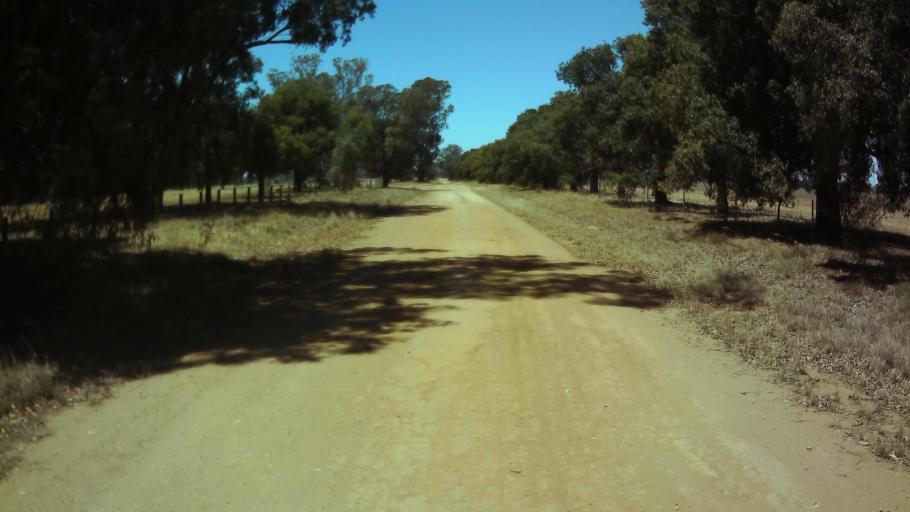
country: AU
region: New South Wales
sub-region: Weddin
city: Grenfell
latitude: -34.0447
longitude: 147.8058
